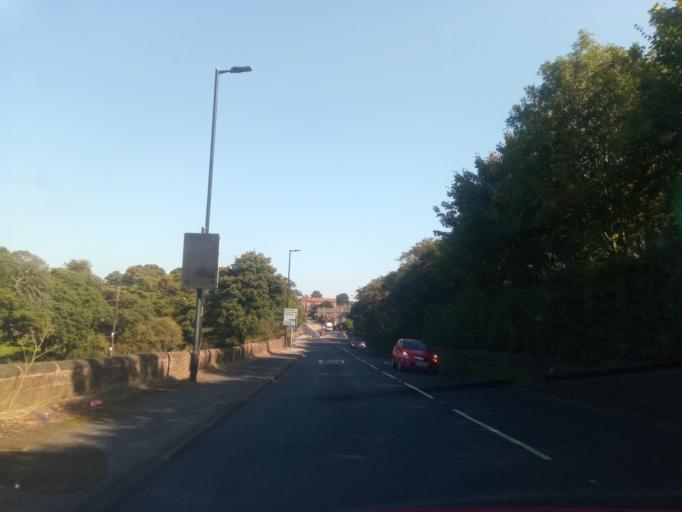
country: GB
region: England
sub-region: Doncaster
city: Conisbrough
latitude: 53.4705
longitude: -1.2612
